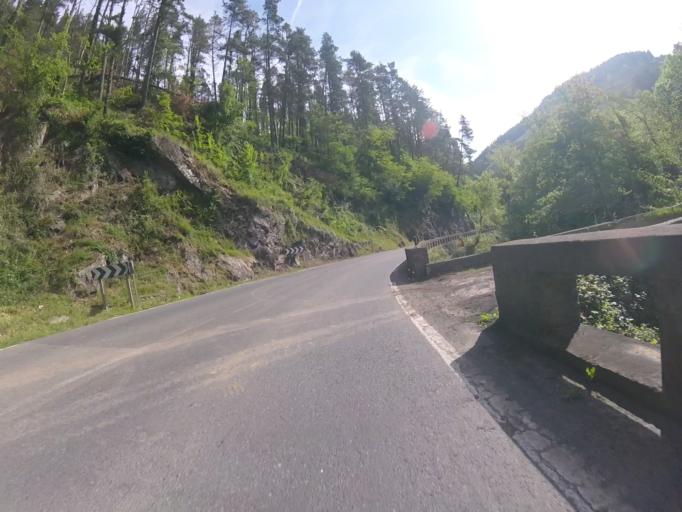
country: ES
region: Basque Country
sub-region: Provincia de Guipuzcoa
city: Azkoitia
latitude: 43.1529
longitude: -2.3445
